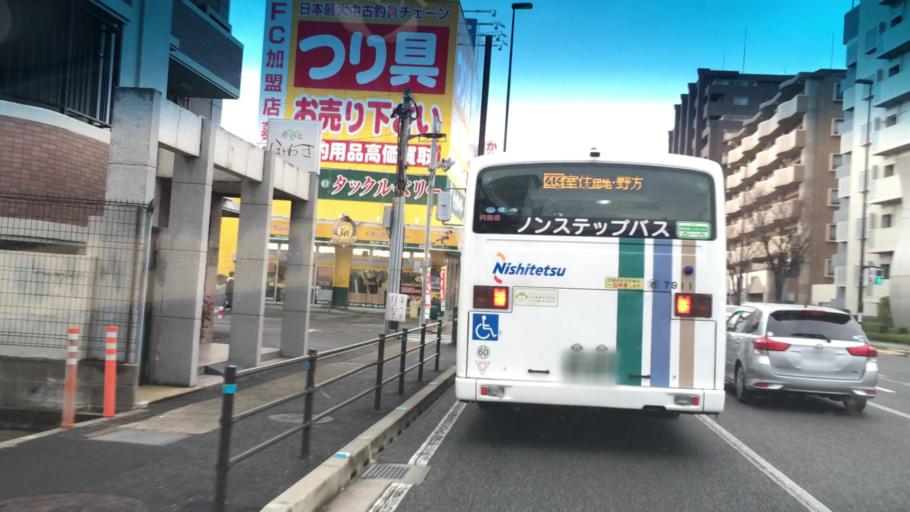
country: JP
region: Fukuoka
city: Fukuoka-shi
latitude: 33.5672
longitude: 130.3403
